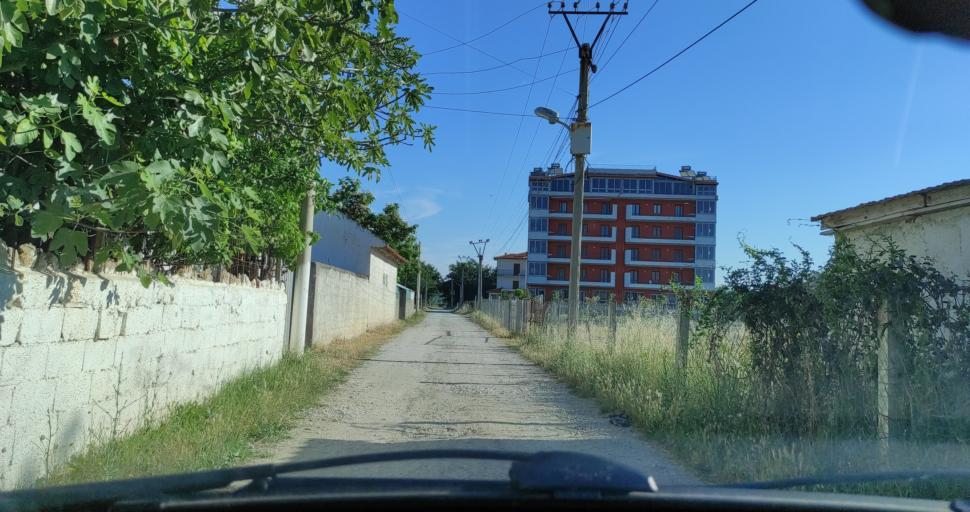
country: AL
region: Shkoder
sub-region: Rrethi i Shkodres
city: Velipoje
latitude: 41.8679
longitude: 19.4261
